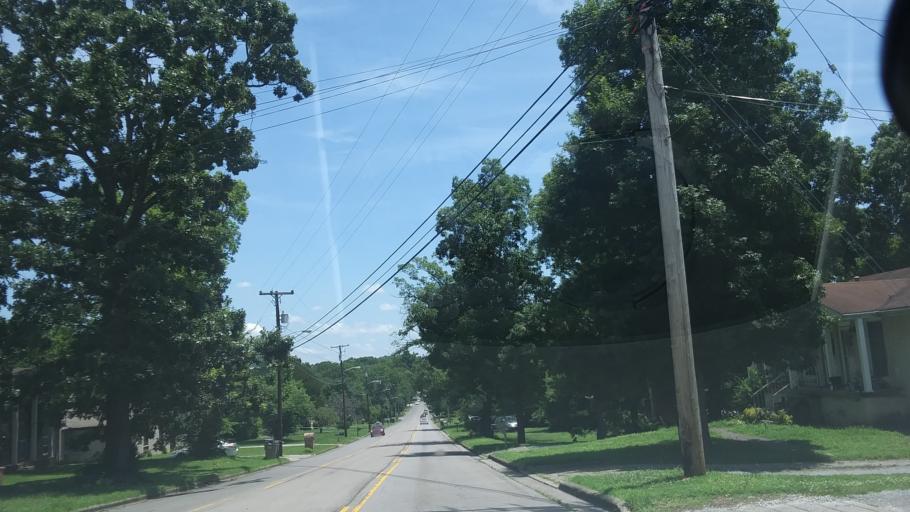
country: US
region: Tennessee
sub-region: Rutherford County
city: La Vergne
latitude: 36.0743
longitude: -86.6285
